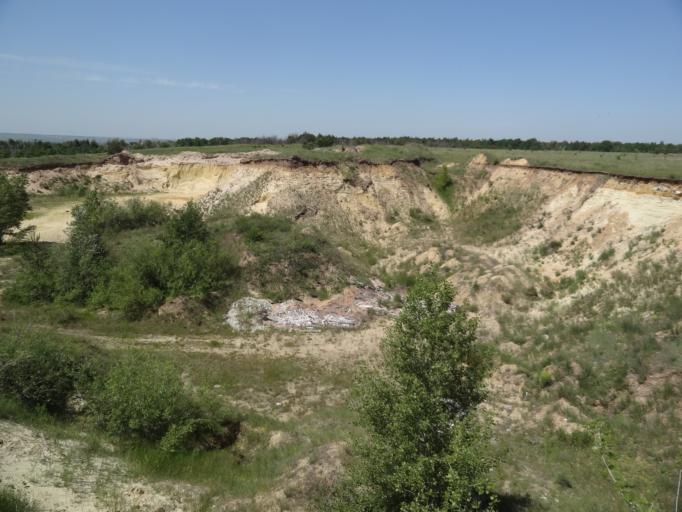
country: RU
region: Saratov
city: Krasnyy Oktyabr'
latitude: 51.2978
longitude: 45.5377
